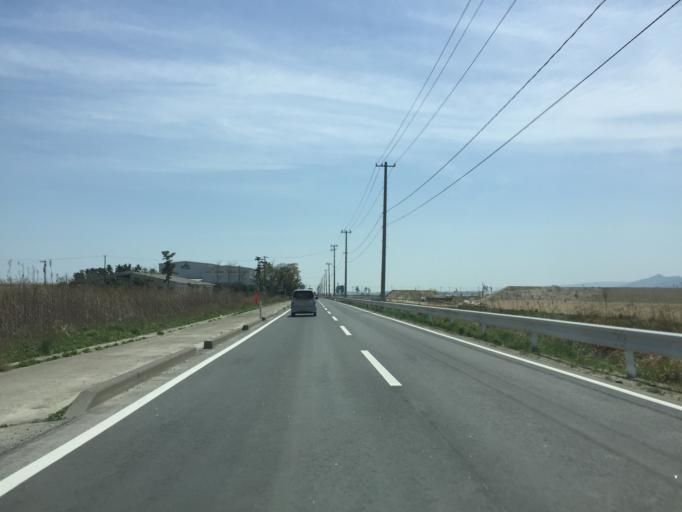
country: JP
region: Miyagi
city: Watari
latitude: 37.9651
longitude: 140.9079
